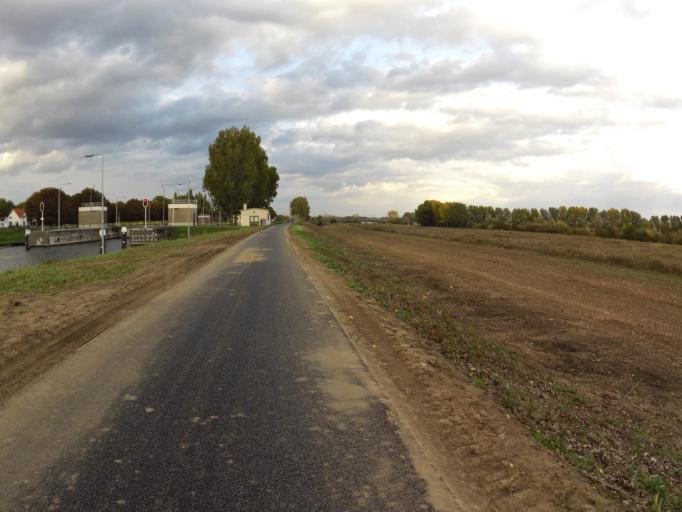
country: NL
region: Limburg
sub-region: Gemeente Maasgouw
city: Maasbracht
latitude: 51.1740
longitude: 5.9235
